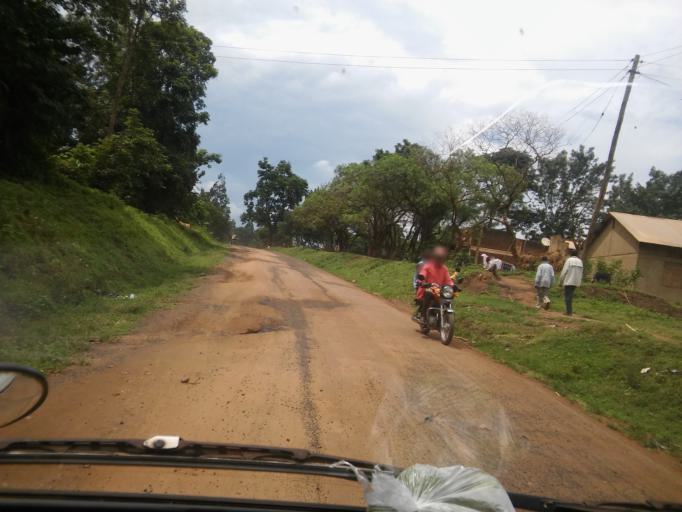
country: UG
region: Eastern Region
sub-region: Bududa District
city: Bududa
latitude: 0.9508
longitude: 34.2654
